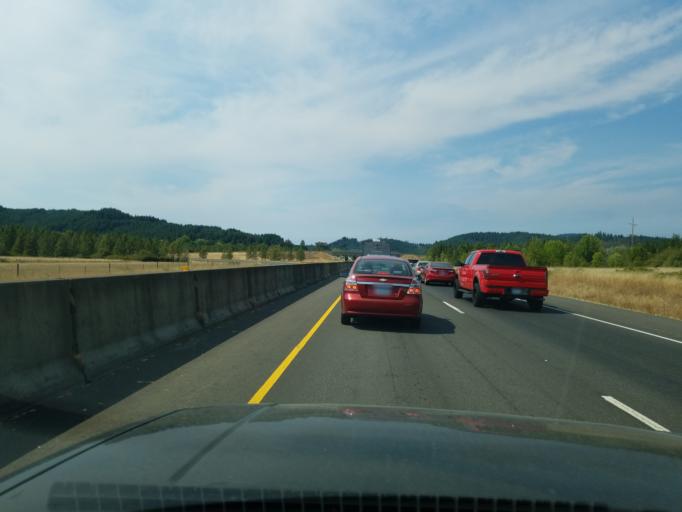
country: US
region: Oregon
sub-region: Yamhill County
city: Willamina
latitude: 45.0525
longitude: -123.5371
